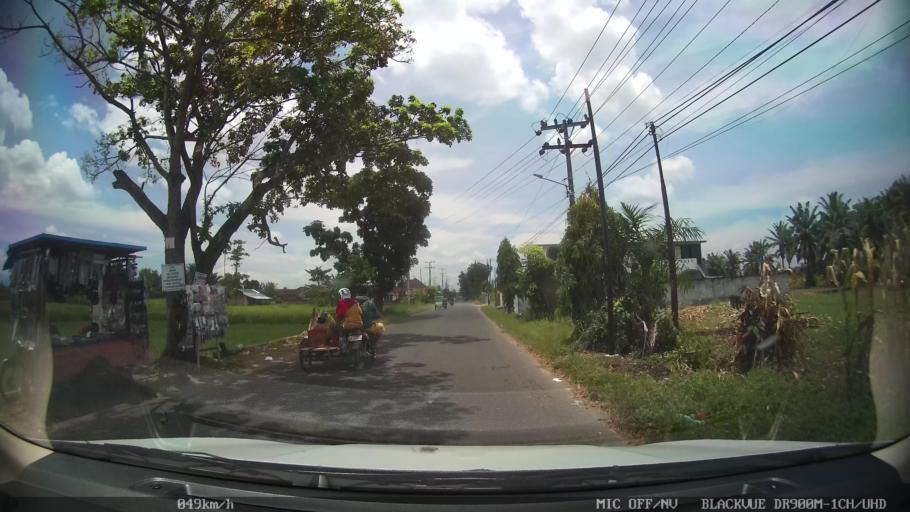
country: ID
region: North Sumatra
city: Binjai
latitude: 3.6279
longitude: 98.5157
